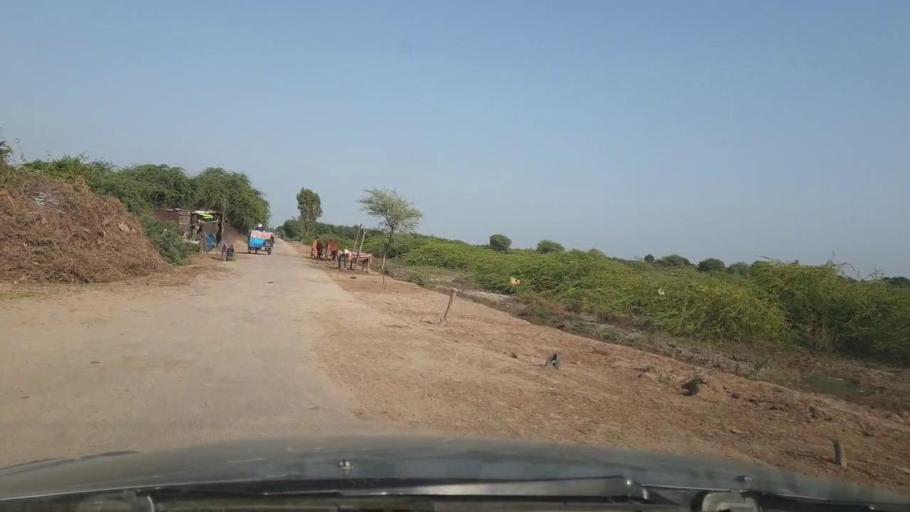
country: PK
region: Sindh
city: Tando Ghulam Ali
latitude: 25.2095
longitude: 68.9469
